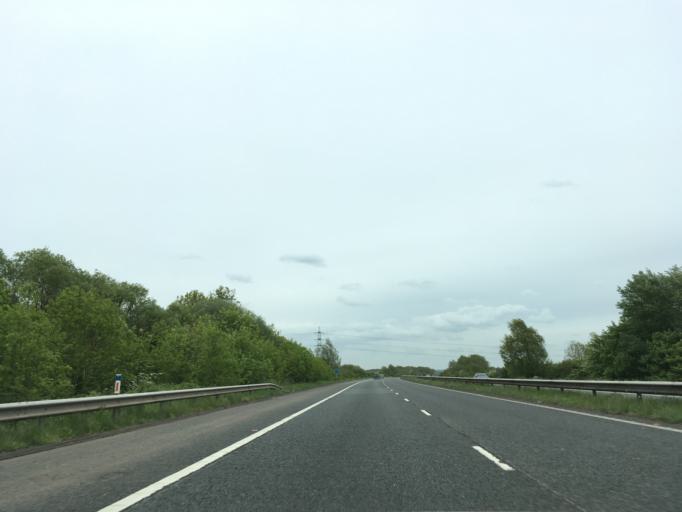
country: GB
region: England
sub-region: South Gloucestershire
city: Severn Beach
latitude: 51.5292
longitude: -2.6505
